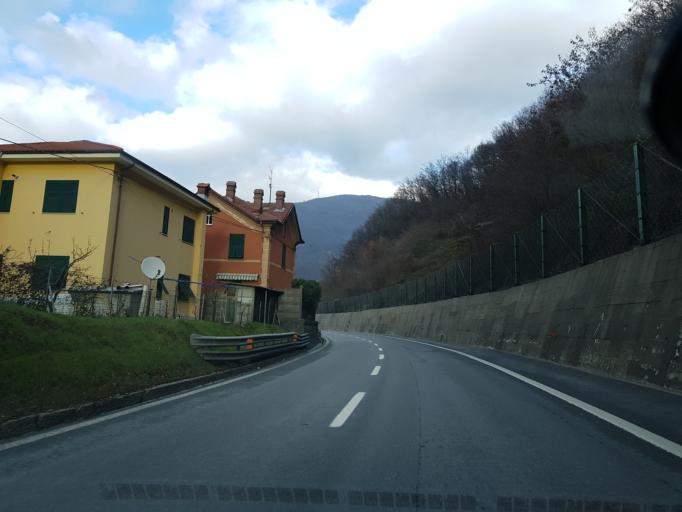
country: IT
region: Liguria
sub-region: Provincia di Genova
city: Isola del Cantone
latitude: 44.6414
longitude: 8.9572
